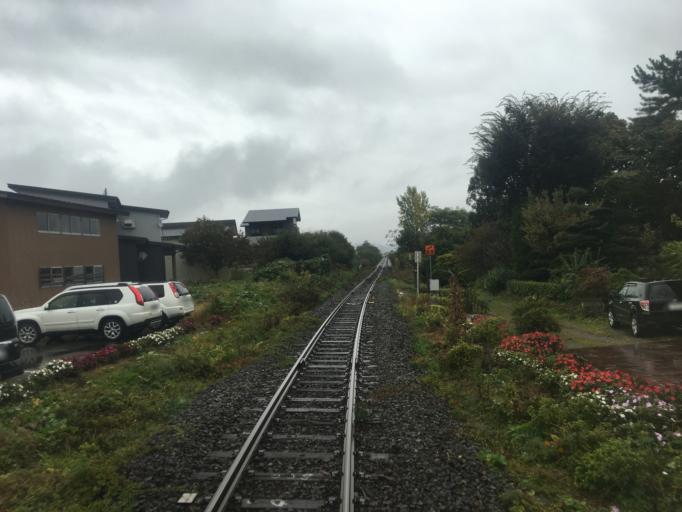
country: JP
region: Yamagata
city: Shinjo
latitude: 38.7659
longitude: 140.4797
